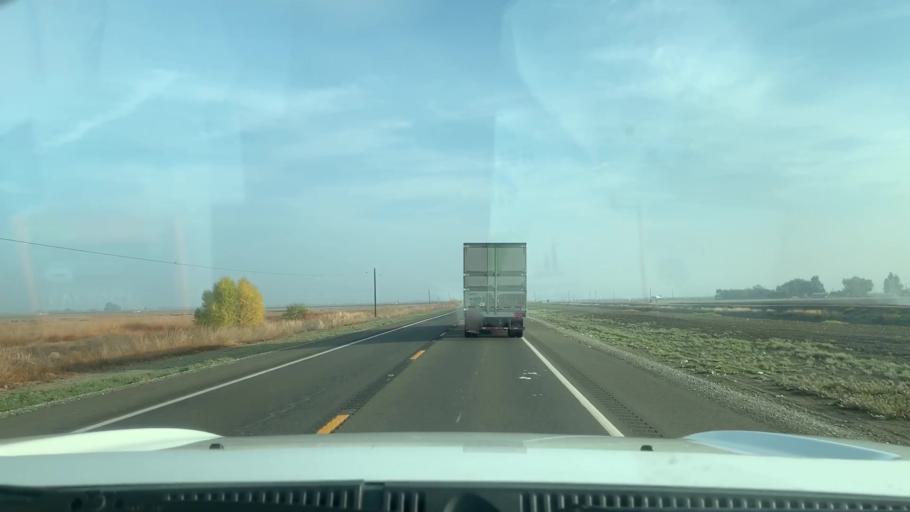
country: US
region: California
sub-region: Kings County
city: Stratford
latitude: 36.1545
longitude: -119.8591
